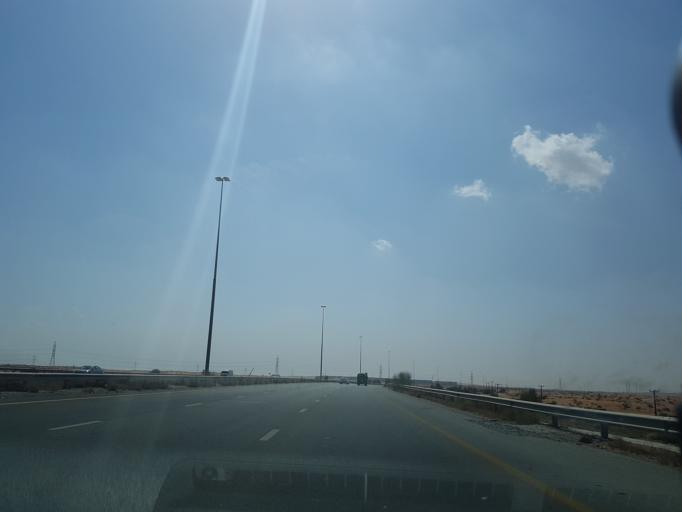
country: AE
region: Ra's al Khaymah
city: Ras al-Khaimah
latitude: 25.6815
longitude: 55.8833
